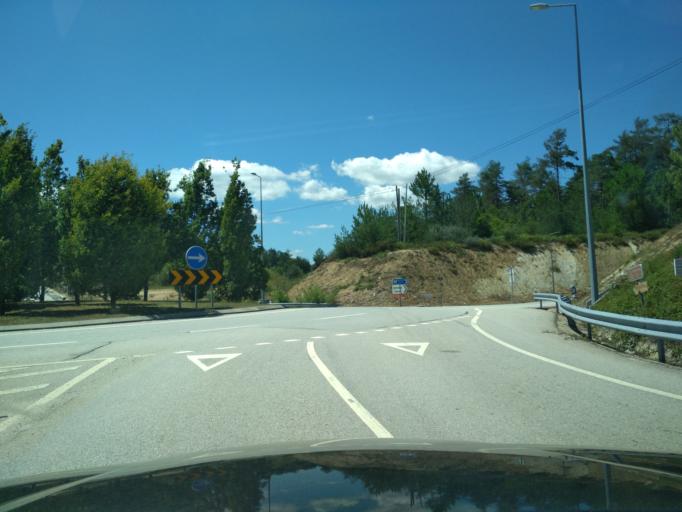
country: PT
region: Vila Real
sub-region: Ribeira de Pena
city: Ribeira de Pena
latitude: 41.5031
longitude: -7.8027
